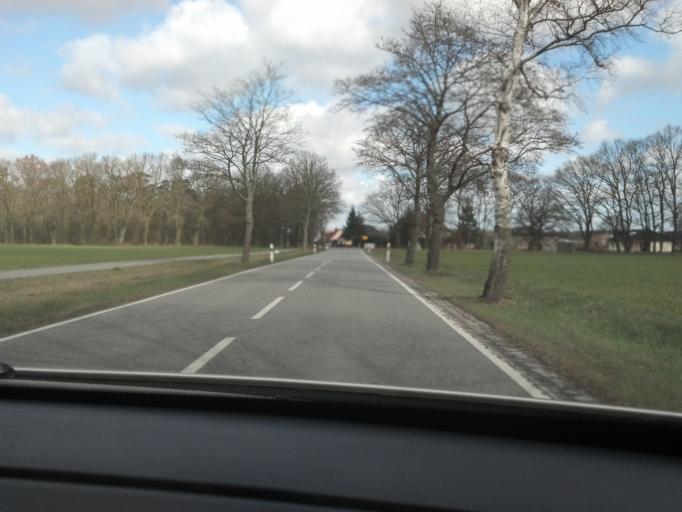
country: DE
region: Mecklenburg-Vorpommern
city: Boizenburg
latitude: 53.3924
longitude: 10.7515
